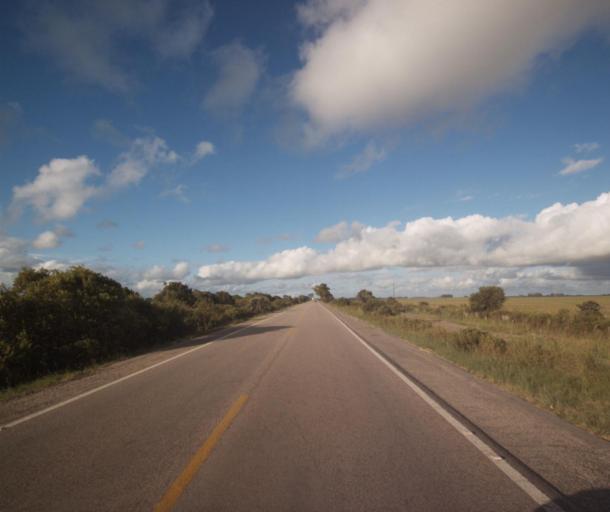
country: BR
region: Rio Grande do Sul
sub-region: Rio Grande
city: Rio Grande
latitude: -32.1803
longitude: -52.4227
